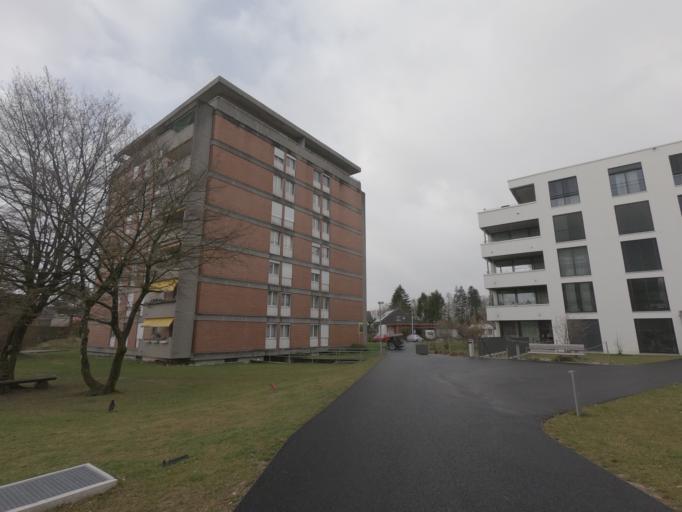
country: CH
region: Solothurn
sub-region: Bezirk Wasseramt
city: Zuchwil
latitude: 47.2140
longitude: 7.5610
